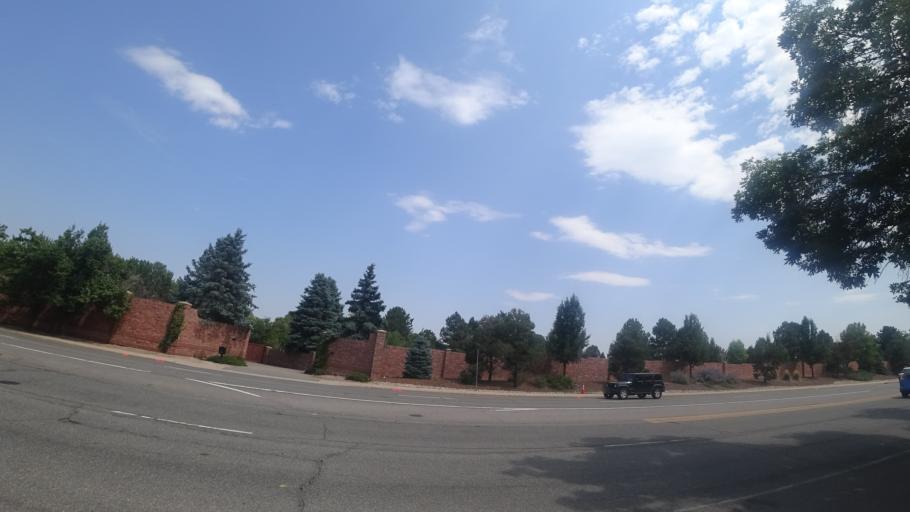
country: US
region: Colorado
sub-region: Arapahoe County
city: Greenwood Village
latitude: 39.6135
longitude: -104.9602
